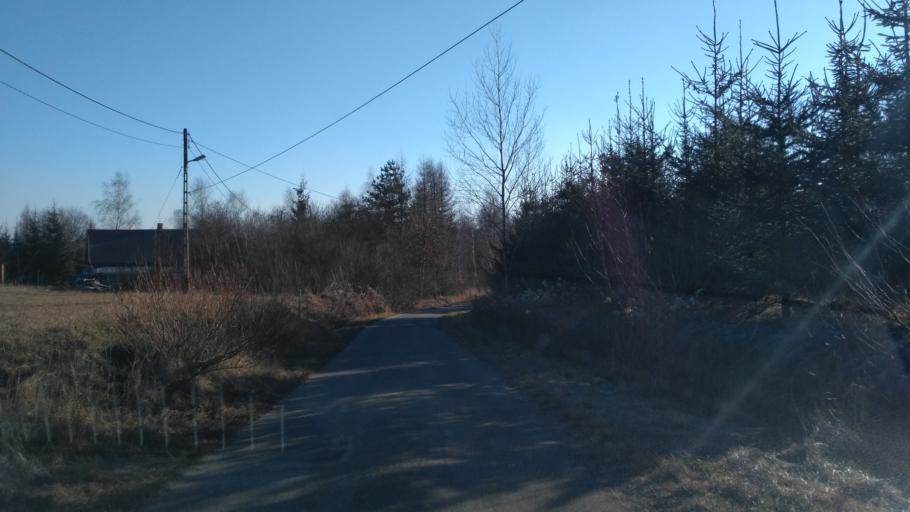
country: PL
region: Subcarpathian Voivodeship
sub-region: Powiat krosnienski
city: Rymanow
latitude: 49.5624
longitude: 21.8904
